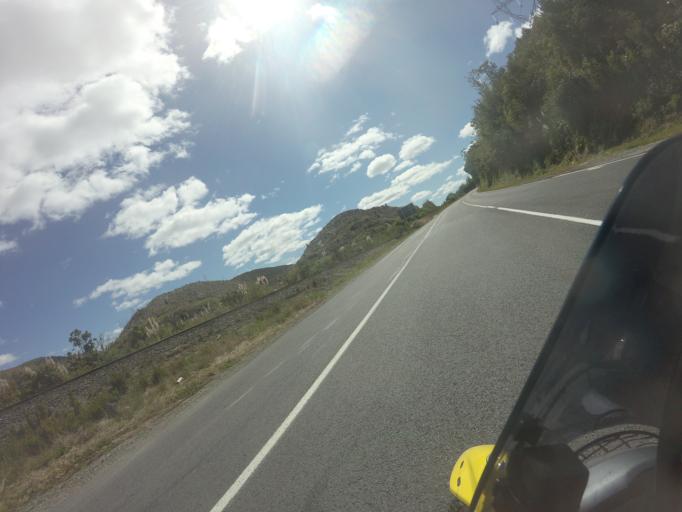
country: NZ
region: Bay of Plenty
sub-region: Kawerau District
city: Kawerau
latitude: -38.1635
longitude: 176.8047
